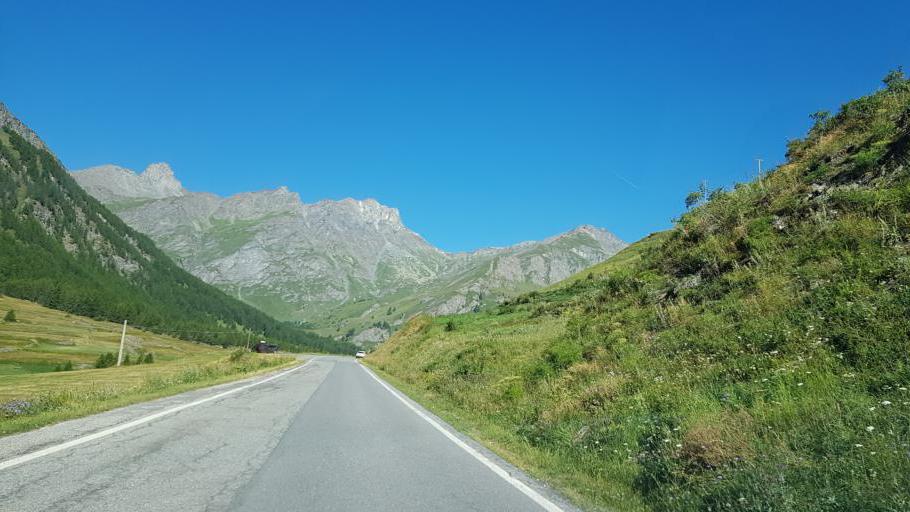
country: IT
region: Piedmont
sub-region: Provincia di Cuneo
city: Pontechianale
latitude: 44.6411
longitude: 7.0092
